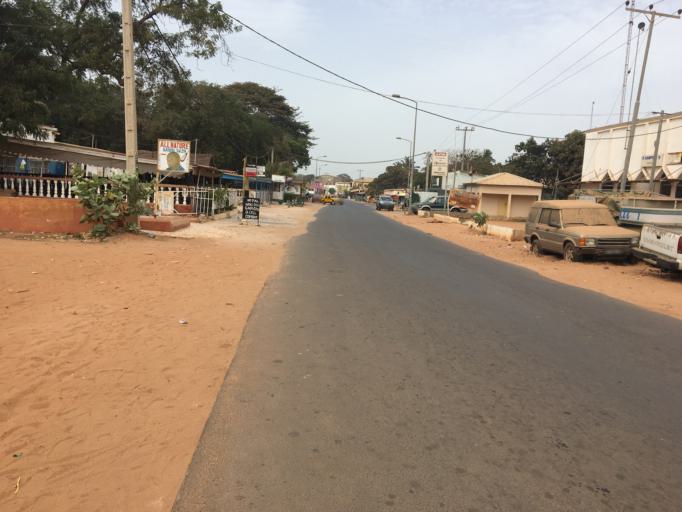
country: GM
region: Banjul
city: Bakau
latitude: 13.4801
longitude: -16.6791
